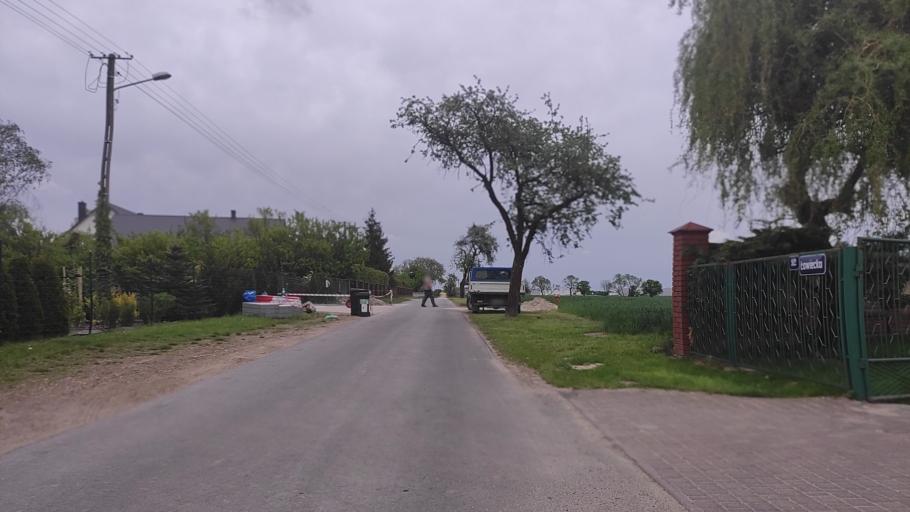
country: PL
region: Greater Poland Voivodeship
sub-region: Powiat poznanski
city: Swarzedz
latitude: 52.4097
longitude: 17.1315
